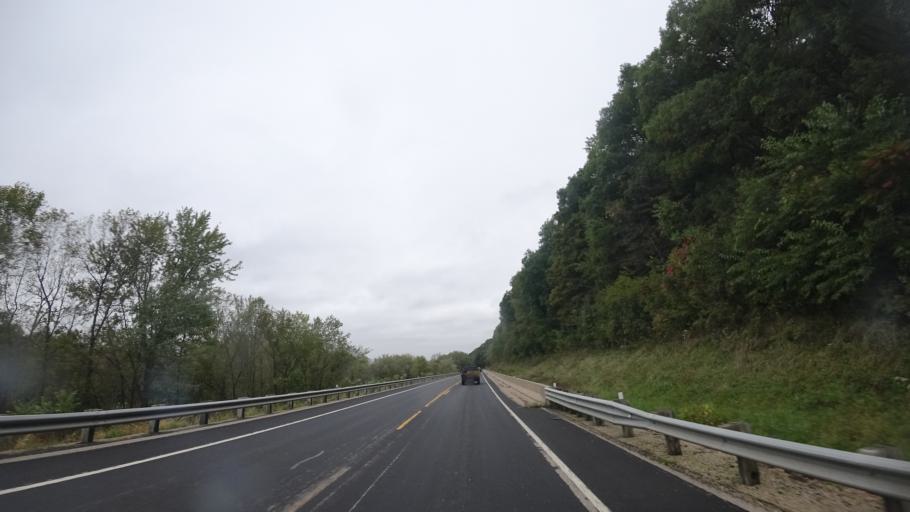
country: US
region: Wisconsin
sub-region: Grant County
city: Boscobel
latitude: 43.1311
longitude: -90.7548
